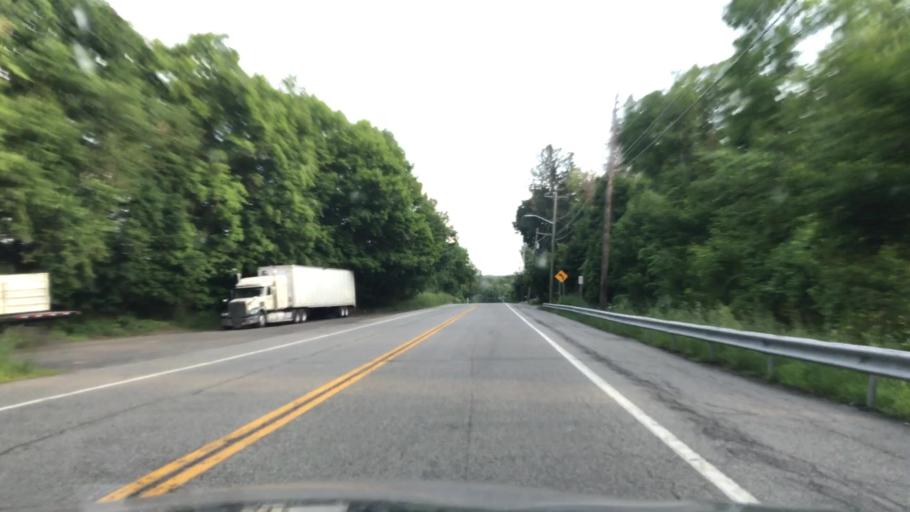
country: US
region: New York
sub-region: Orange County
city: Harriman
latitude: 41.3063
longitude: -74.1457
